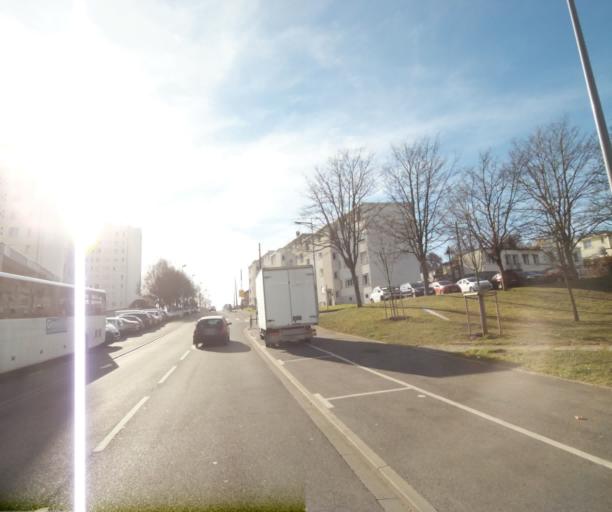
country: FR
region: Lorraine
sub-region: Departement de Meurthe-et-Moselle
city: Vandoeuvre-les-Nancy
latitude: 48.6611
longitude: 6.1692
